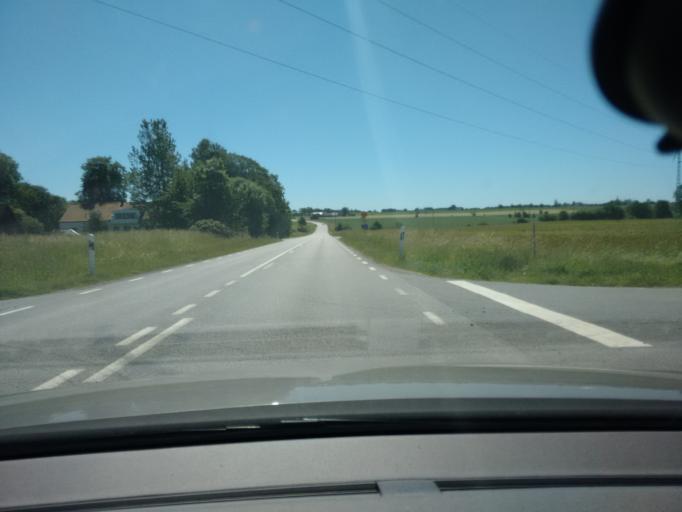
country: SE
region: Skane
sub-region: Horby Kommun
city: Hoerby
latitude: 55.8299
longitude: 13.6598
